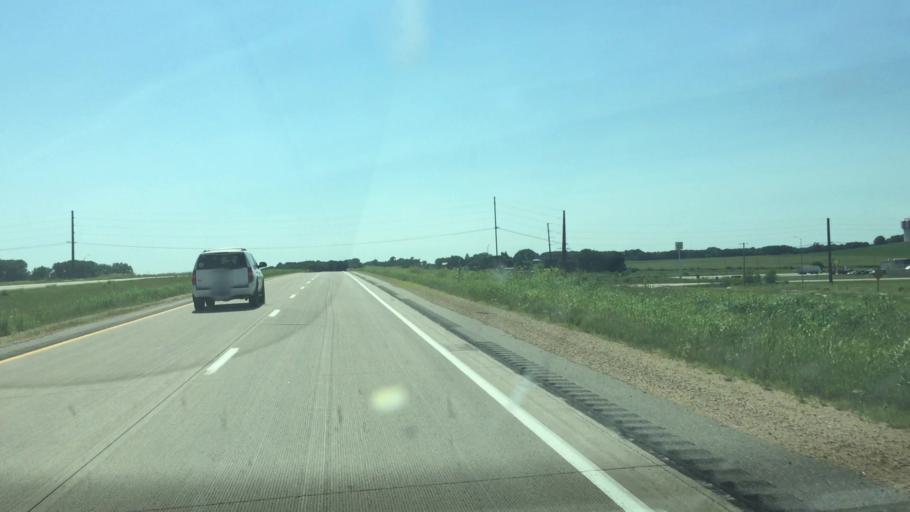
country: US
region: Iowa
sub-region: Jones County
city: Monticello
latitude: 42.2079
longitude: -91.1858
